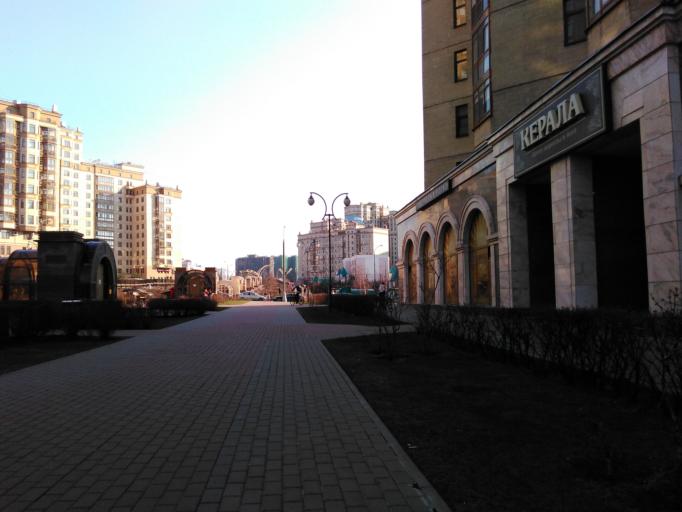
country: RU
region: Moscow
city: Ramenki
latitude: 55.7042
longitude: 37.5137
